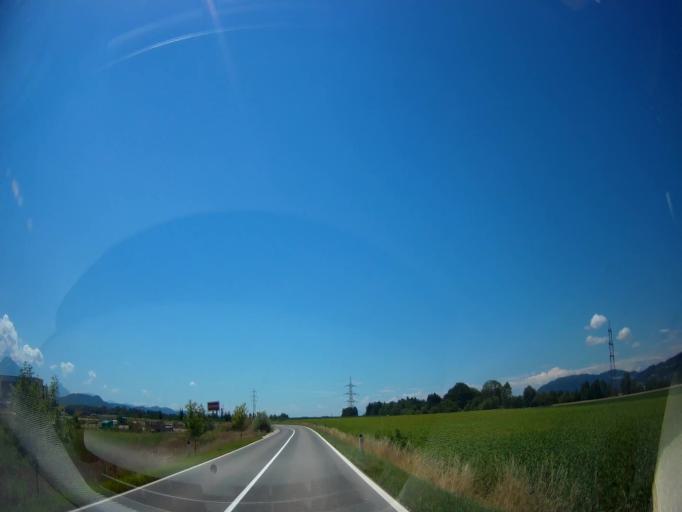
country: AT
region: Carinthia
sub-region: Politischer Bezirk Volkermarkt
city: Voelkermarkt
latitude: 46.6264
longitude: 14.6231
